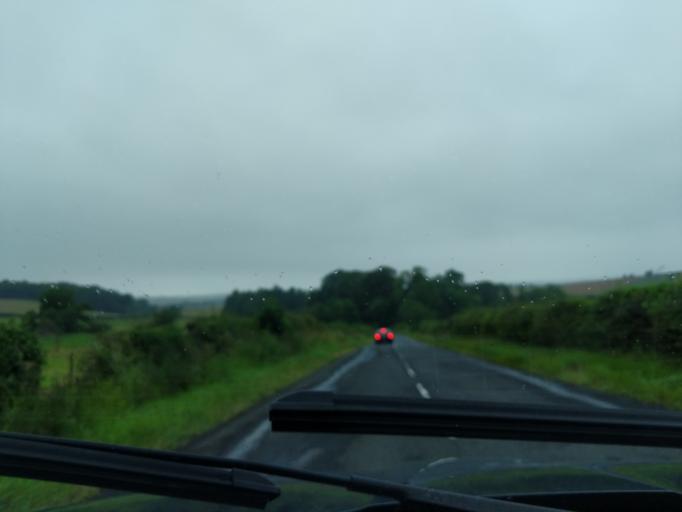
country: GB
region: England
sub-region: Northumberland
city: Lowick
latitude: 55.6596
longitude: -1.9268
